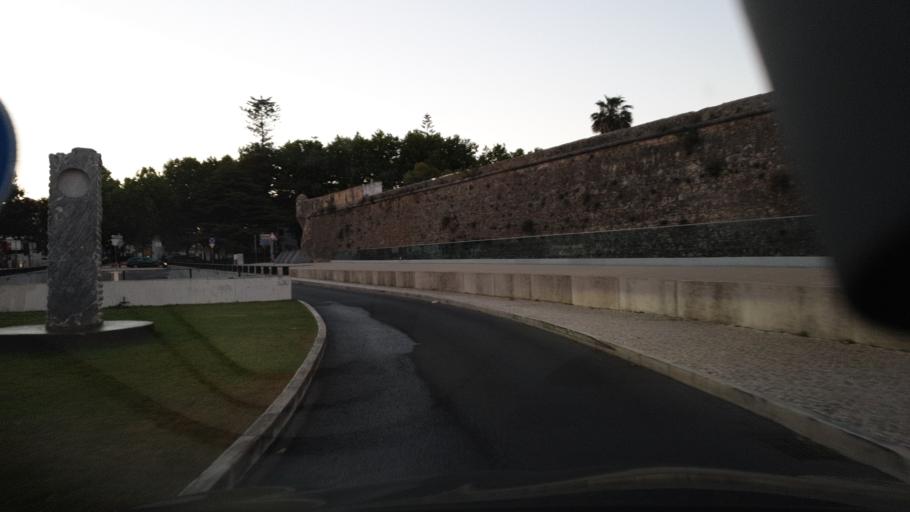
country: PT
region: Lisbon
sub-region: Cascais
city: Cascais
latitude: 38.6935
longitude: -9.4206
